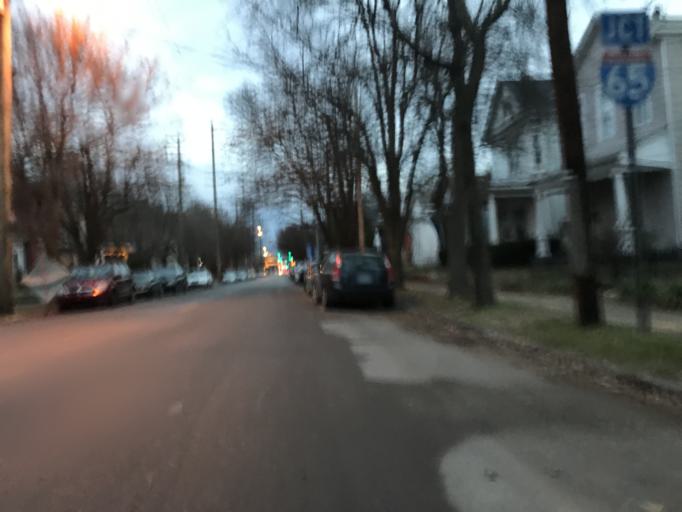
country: US
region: Kentucky
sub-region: Jefferson County
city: Louisville
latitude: 38.2329
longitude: -85.7519
